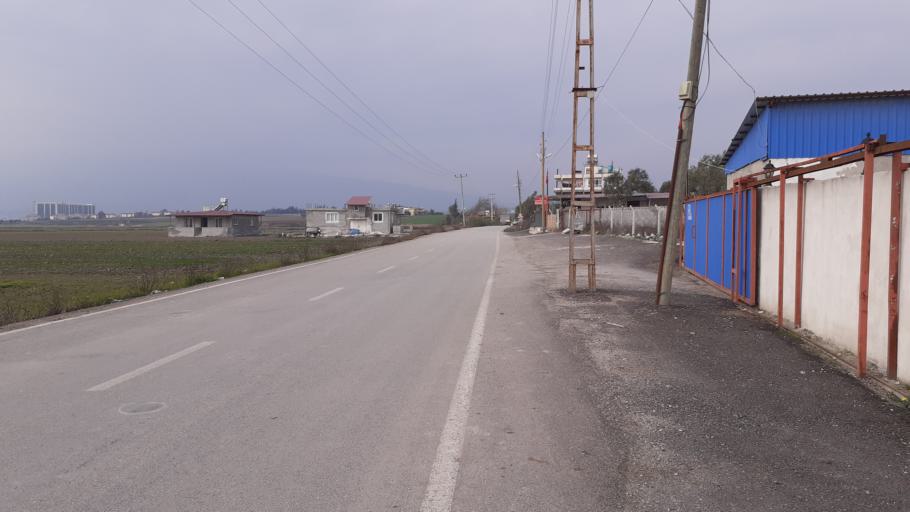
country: TR
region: Hatay
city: Kastal
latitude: 36.2633
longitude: 36.2420
